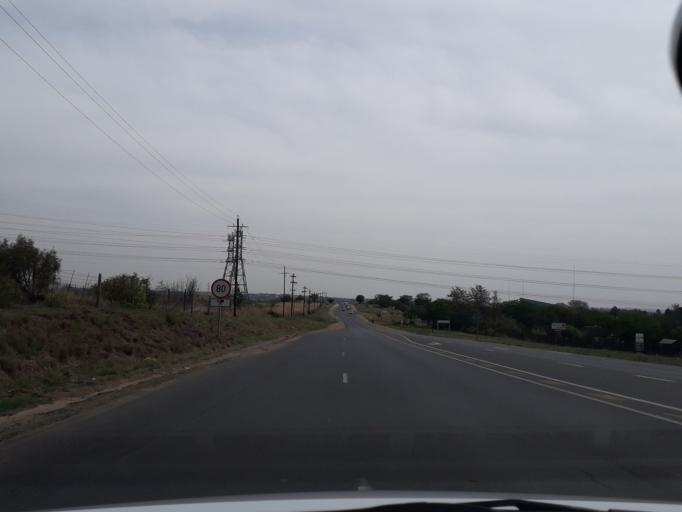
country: ZA
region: Gauteng
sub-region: City of Johannesburg Metropolitan Municipality
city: Diepsloot
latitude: -25.9911
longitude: 28.0507
